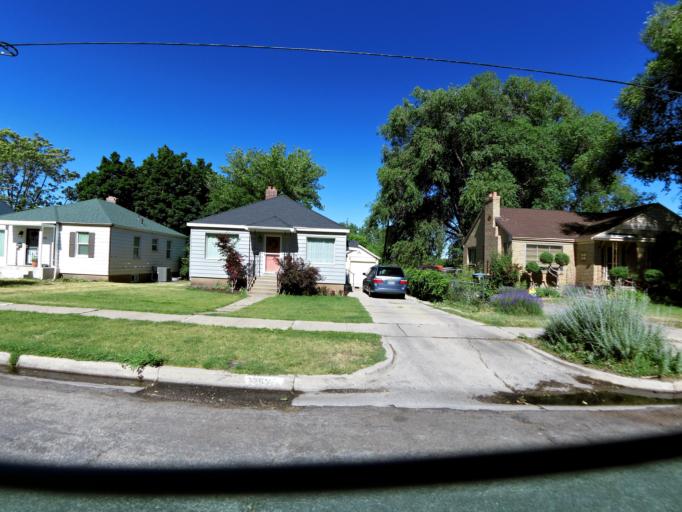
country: US
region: Utah
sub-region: Weber County
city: Ogden
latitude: 41.2253
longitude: -111.9454
